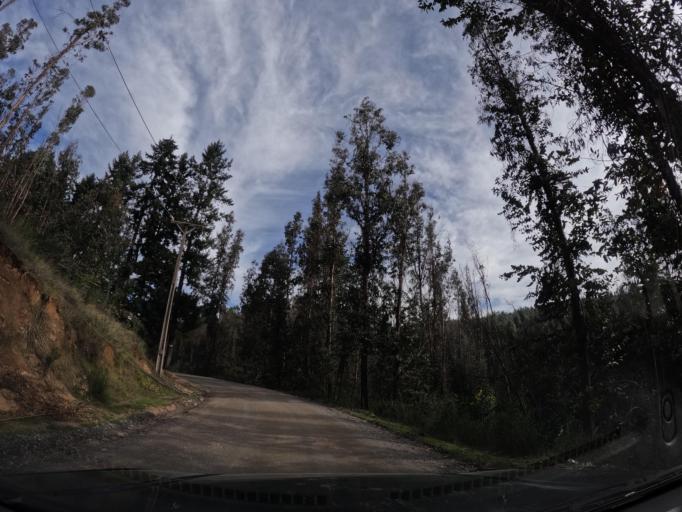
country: CL
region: Biobio
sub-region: Provincia de Concepcion
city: Chiguayante
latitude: -37.0117
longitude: -72.9106
